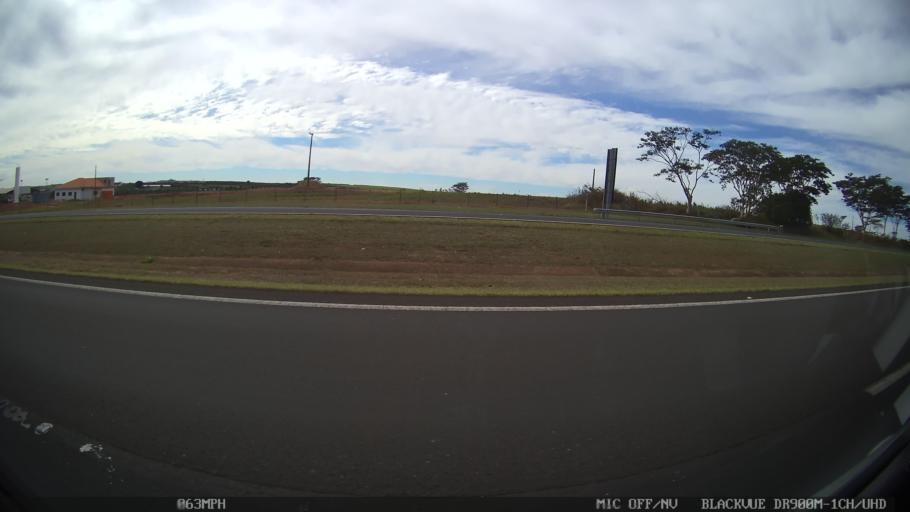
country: BR
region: Sao Paulo
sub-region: Santa Adelia
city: Santa Adelia
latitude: -21.3779
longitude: -48.7399
